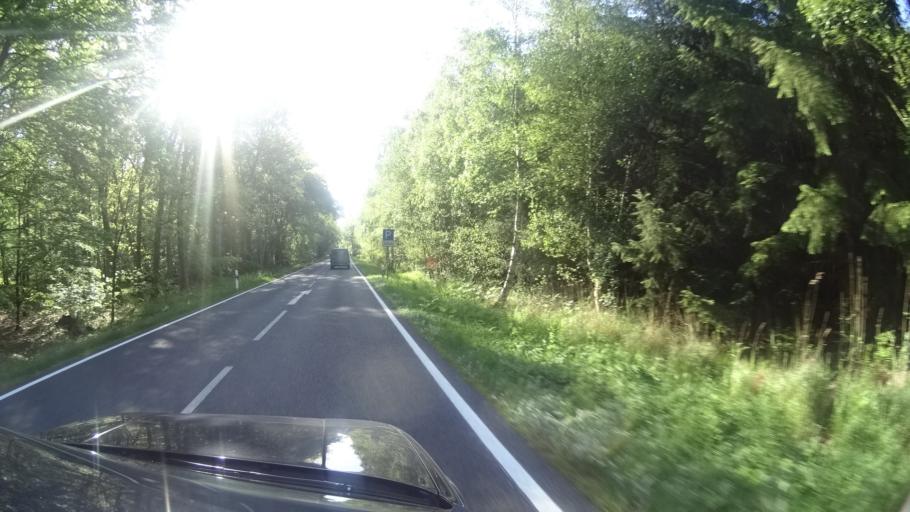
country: DE
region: Mecklenburg-Vorpommern
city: Born
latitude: 54.4031
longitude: 12.4726
